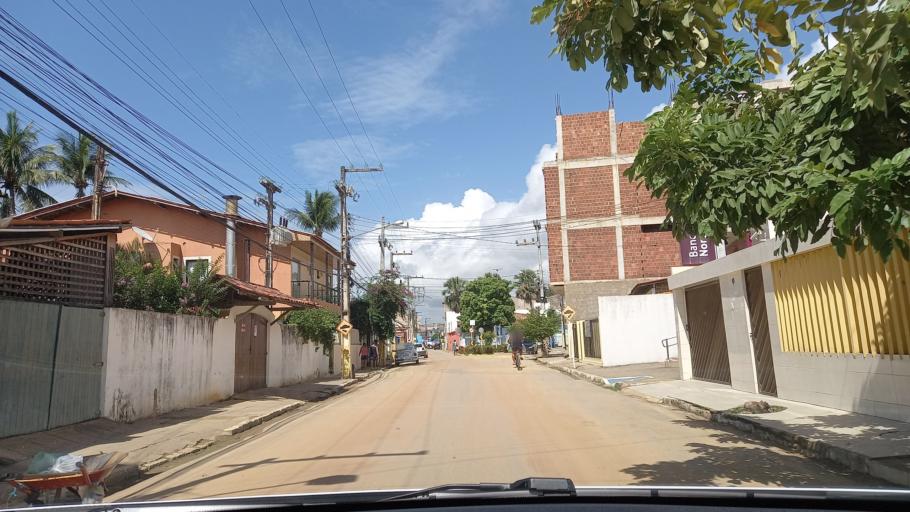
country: BR
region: Alagoas
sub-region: Maragogi
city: Maragogi
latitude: -9.0112
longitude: -35.2203
